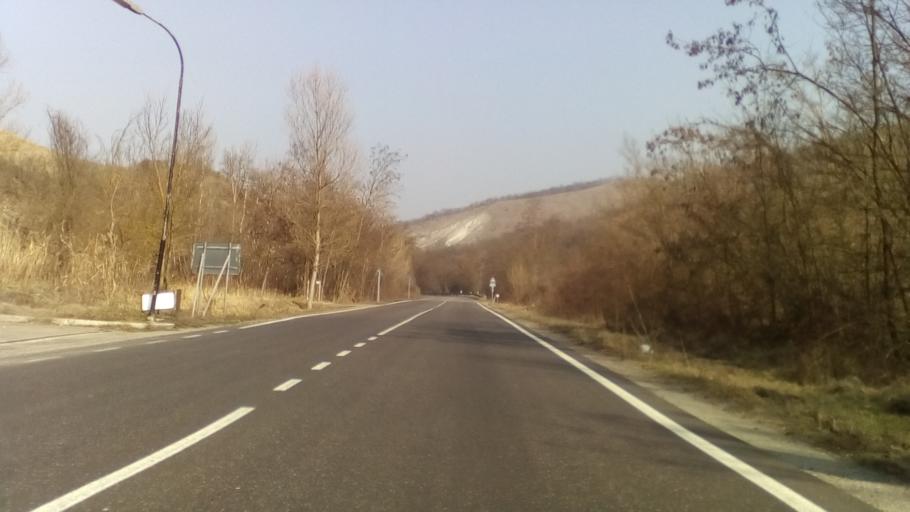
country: IT
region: Emilia-Romagna
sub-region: Provincia di Modena
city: Serramazzoni
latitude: 44.4620
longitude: 10.8346
